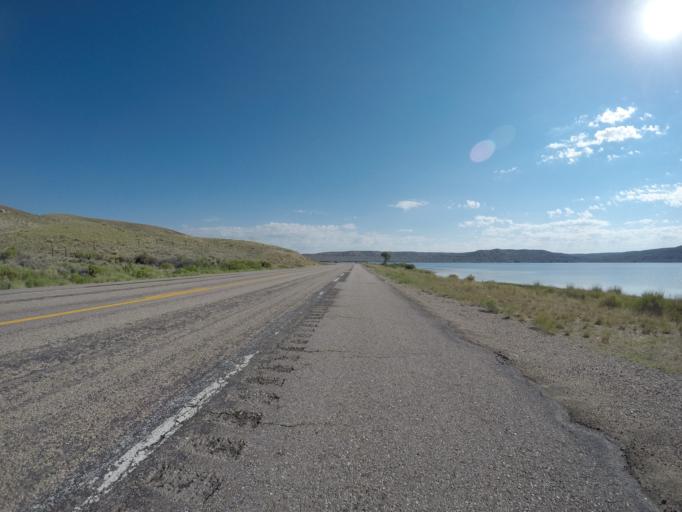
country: US
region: Wyoming
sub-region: Sublette County
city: Marbleton
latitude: 42.1031
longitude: -110.1412
